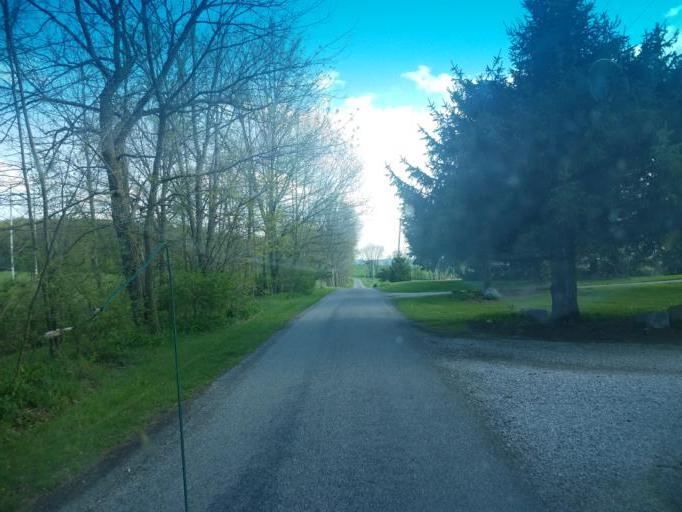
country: US
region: Ohio
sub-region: Wayne County
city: Shreve
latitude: 40.6780
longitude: -81.9335
